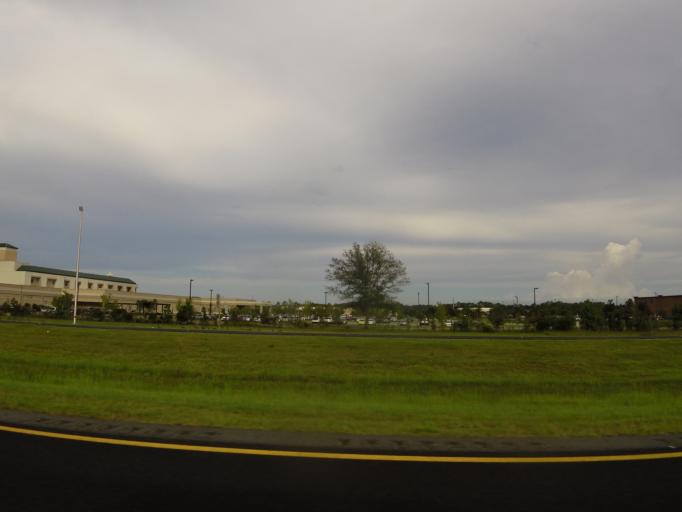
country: US
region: Florida
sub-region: Clay County
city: Middleburg
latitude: 30.1081
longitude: -81.8350
